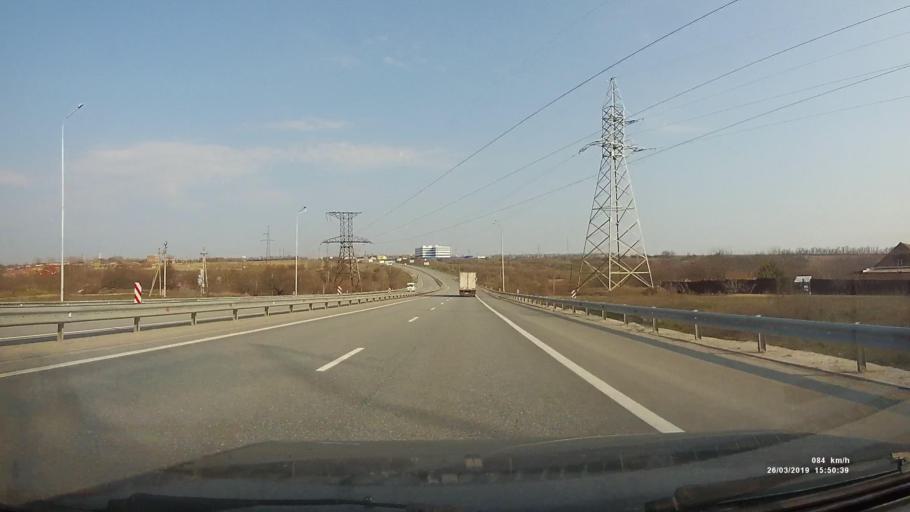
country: RU
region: Rostov
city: Chaltyr
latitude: 47.2724
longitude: 39.4899
